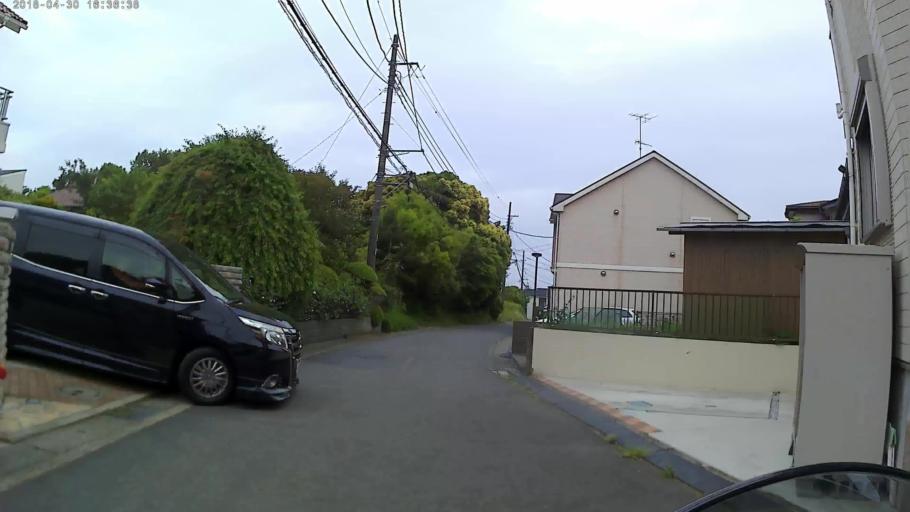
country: JP
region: Kanagawa
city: Atsugi
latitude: 35.4366
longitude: 139.4101
